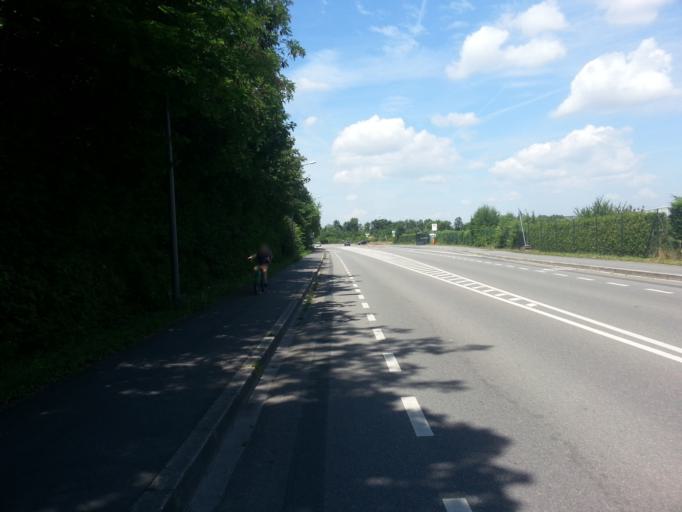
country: DE
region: Baden-Wuerttemberg
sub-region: Karlsruhe Region
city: Eppelheim
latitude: 49.4319
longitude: 8.6428
